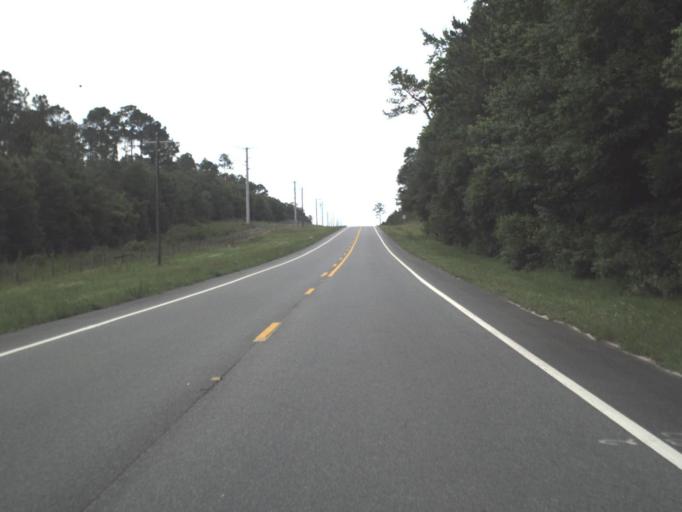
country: US
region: Florida
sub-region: Clay County
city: Middleburg
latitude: 29.9691
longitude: -81.8977
